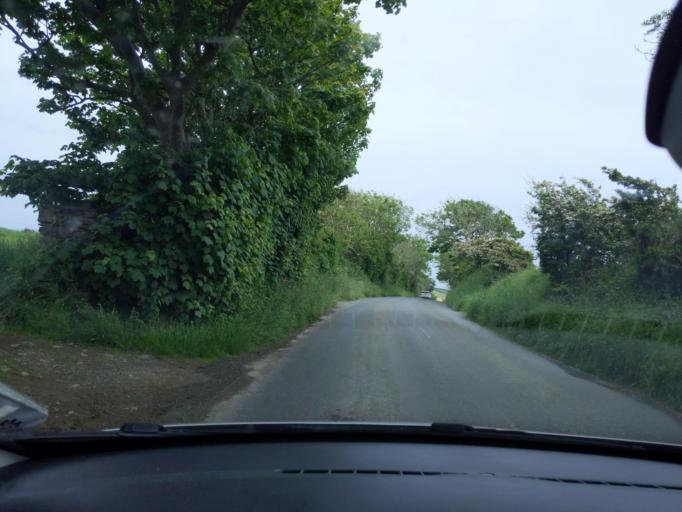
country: IM
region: Douglas
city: Douglas
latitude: 54.1255
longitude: -4.5681
